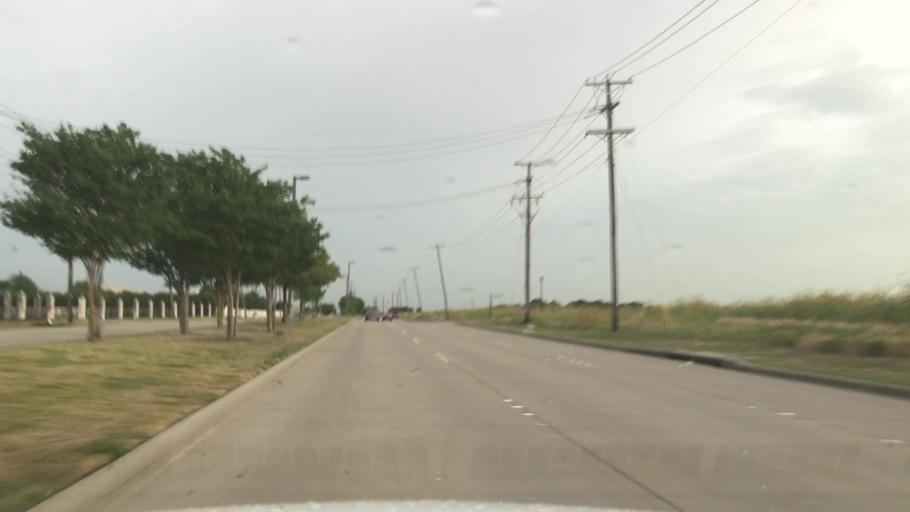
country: US
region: Texas
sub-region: Dallas County
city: Mesquite
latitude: 32.7247
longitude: -96.5476
